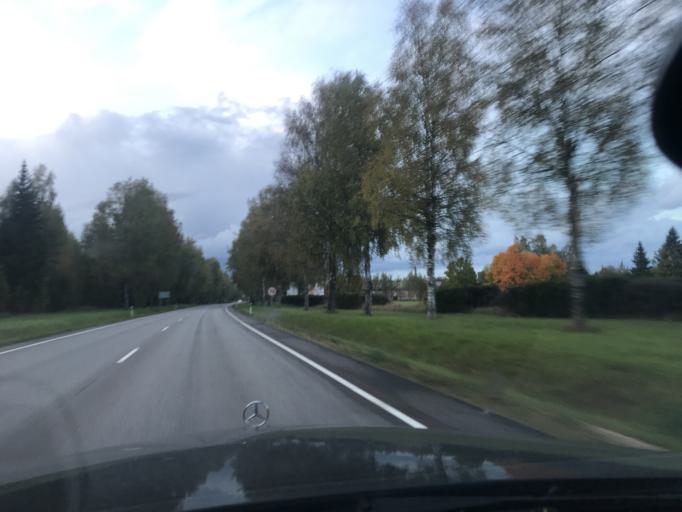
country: EE
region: Valgamaa
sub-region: Torva linn
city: Torva
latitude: 57.9868
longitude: 25.9421
